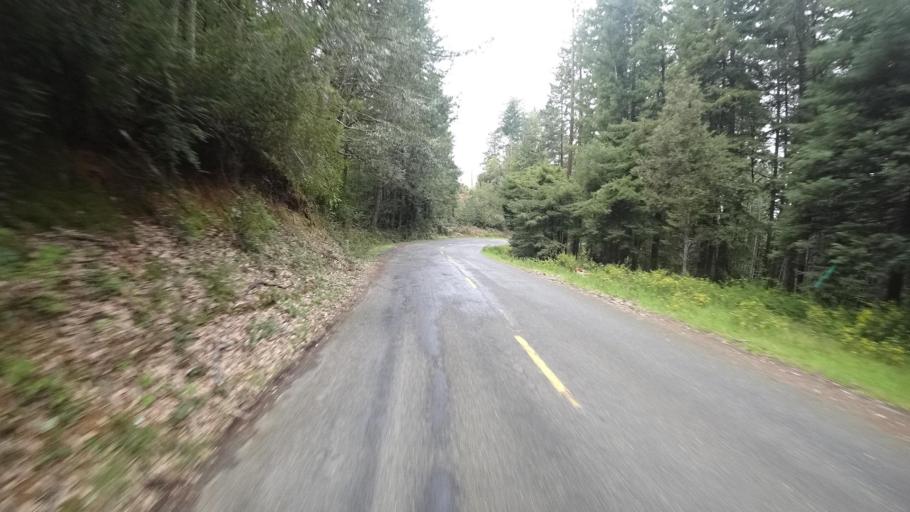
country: US
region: California
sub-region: Humboldt County
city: Redway
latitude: 40.2776
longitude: -123.7913
